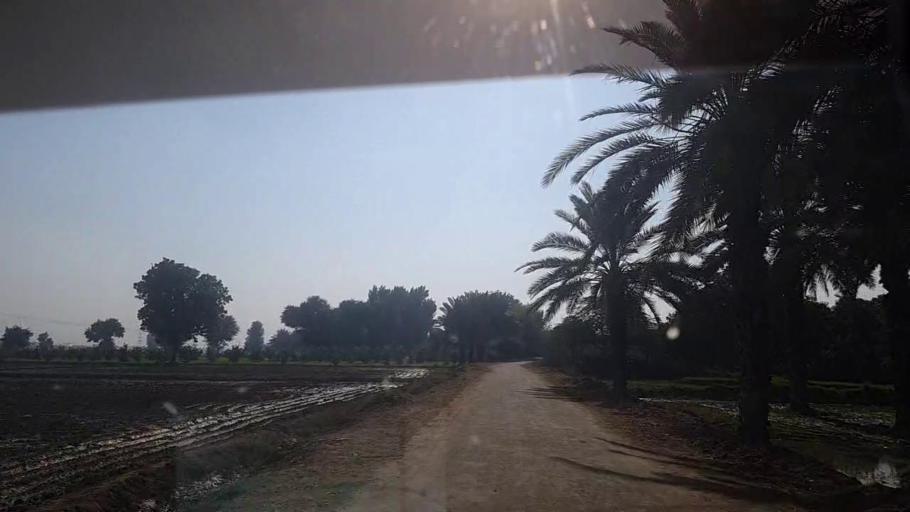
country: PK
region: Sindh
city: Gambat
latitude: 27.3888
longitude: 68.5996
